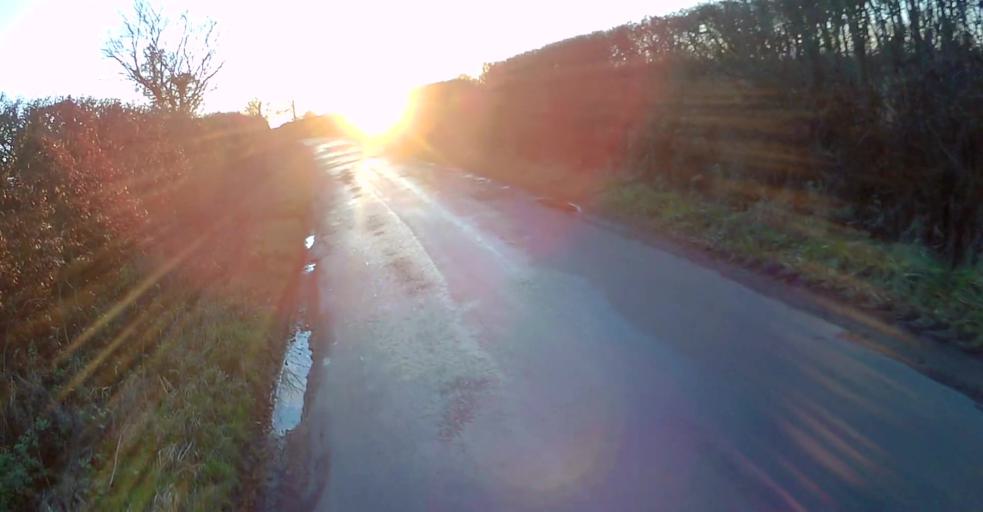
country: GB
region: England
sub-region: West Berkshire
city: Stratfield Mortimer
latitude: 51.3472
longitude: -1.0304
